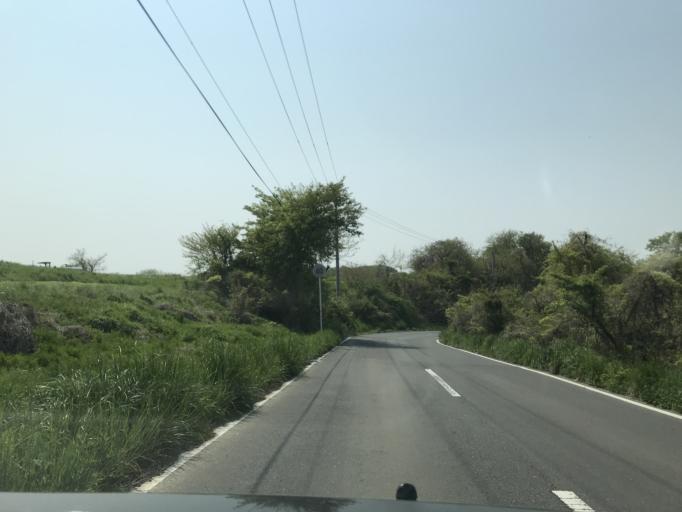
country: JP
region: Iwate
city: Ichinoseki
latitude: 38.8512
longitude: 141.0559
